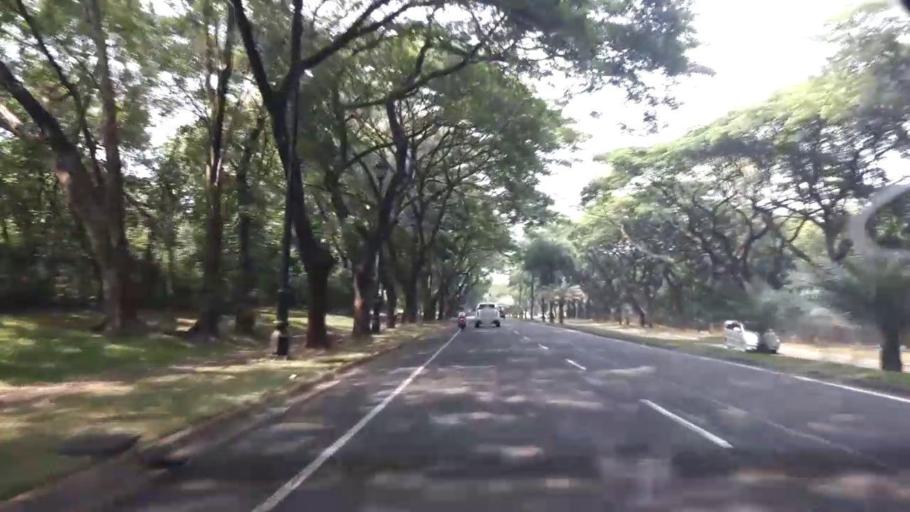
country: ID
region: Banten
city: Tangerang
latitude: -6.2312
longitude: 106.6085
